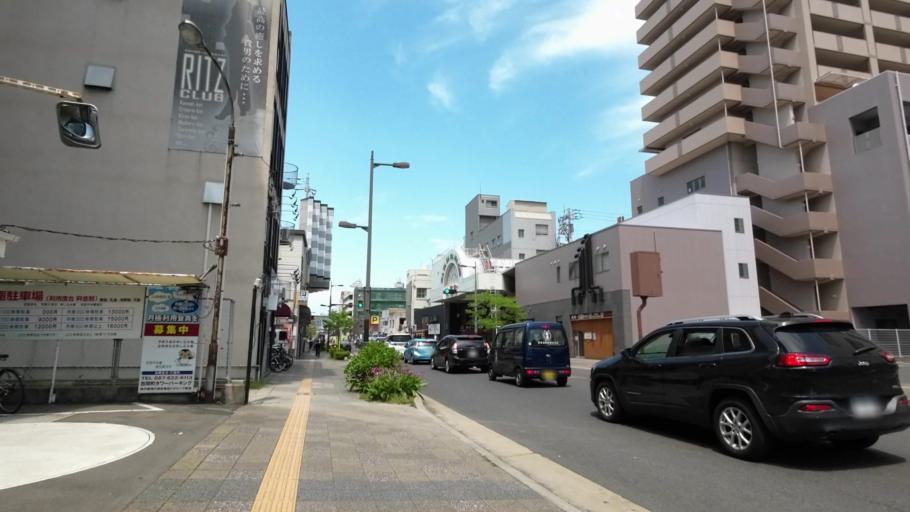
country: JP
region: Kagawa
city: Takamatsu-shi
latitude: 34.3452
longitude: 134.0530
